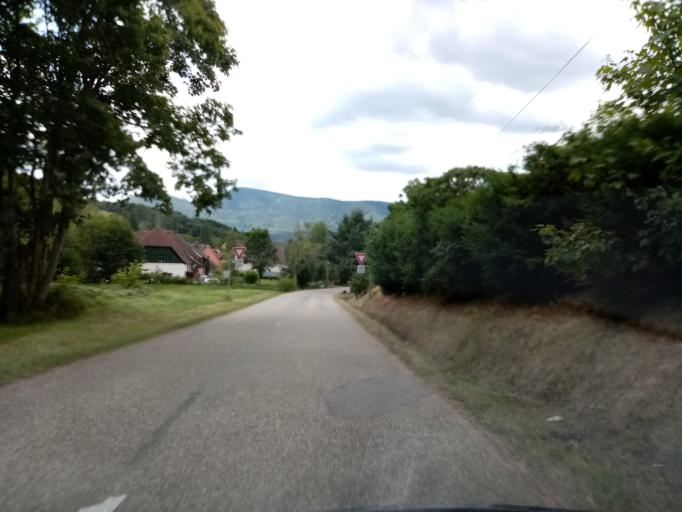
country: FR
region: Alsace
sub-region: Departement du Bas-Rhin
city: Ville
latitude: 48.3269
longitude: 7.3623
